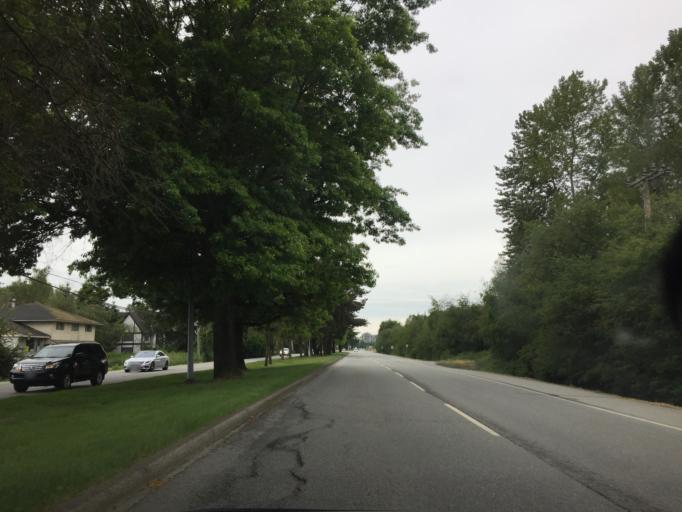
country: CA
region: British Columbia
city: Richmond
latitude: 49.1702
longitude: -123.1097
